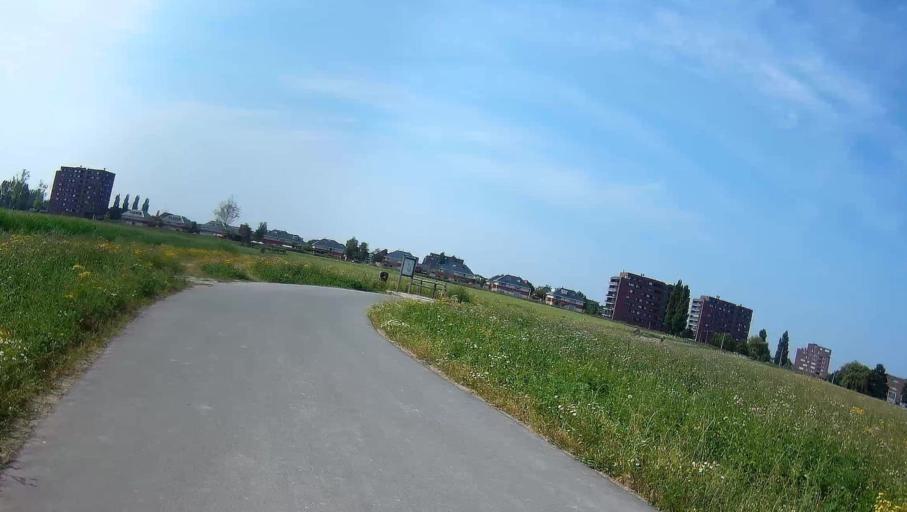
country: NL
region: South Holland
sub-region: Gemeente Pijnacker-Nootdorp
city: Pijnacker
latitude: 52.0613
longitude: 4.4239
